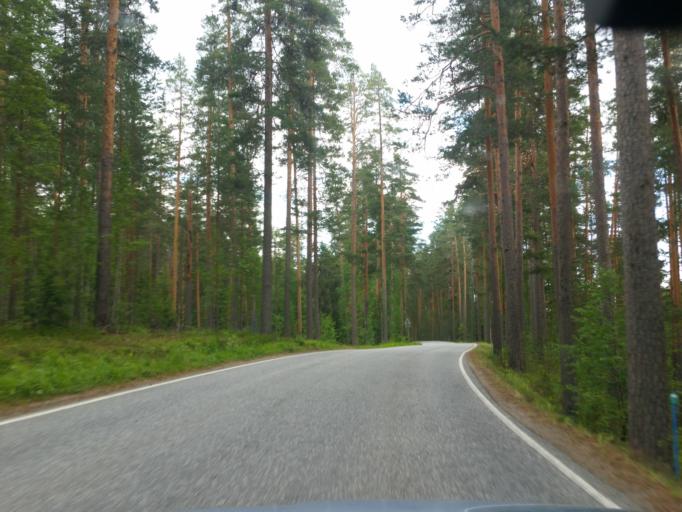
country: FI
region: Southern Savonia
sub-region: Savonlinna
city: Sulkava
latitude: 61.7918
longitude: 28.4234
